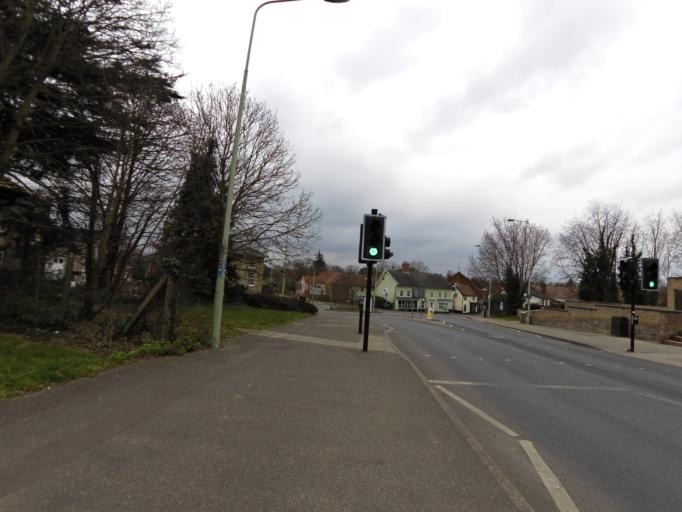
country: GB
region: England
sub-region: Suffolk
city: Halesworth
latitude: 52.3458
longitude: 1.5028
